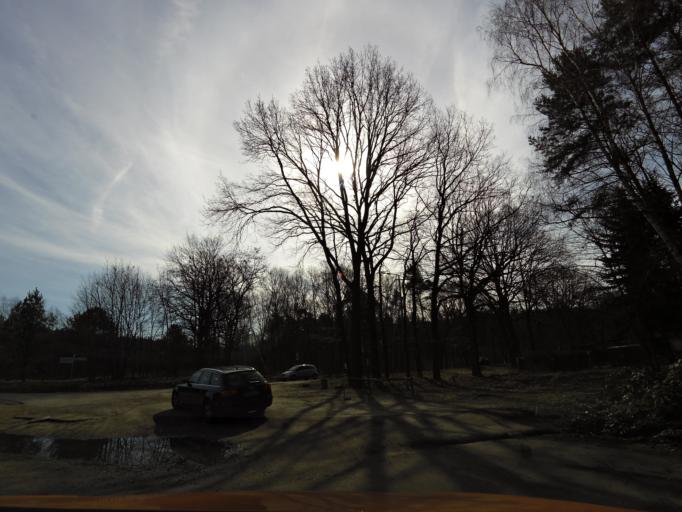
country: DE
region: Brandenburg
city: Michendorf
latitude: 52.3552
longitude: 13.0438
